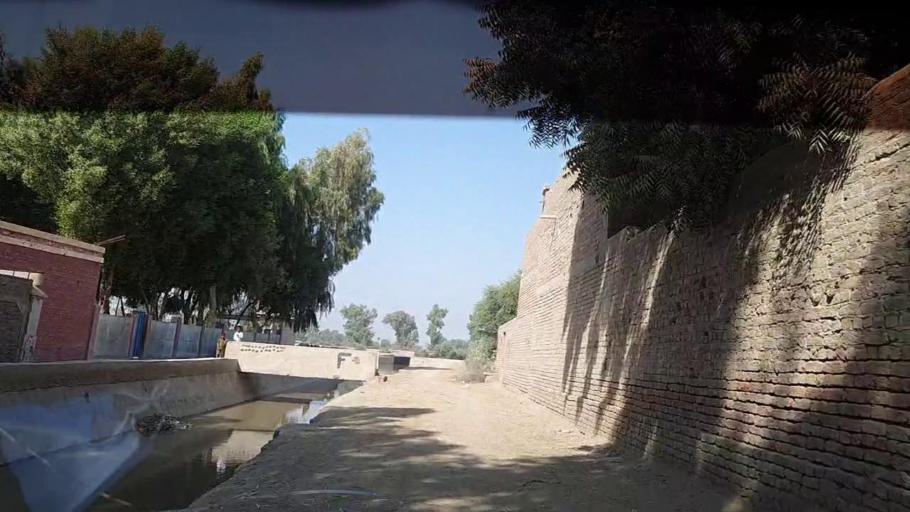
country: PK
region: Sindh
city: Naudero
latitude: 27.6623
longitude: 68.3744
